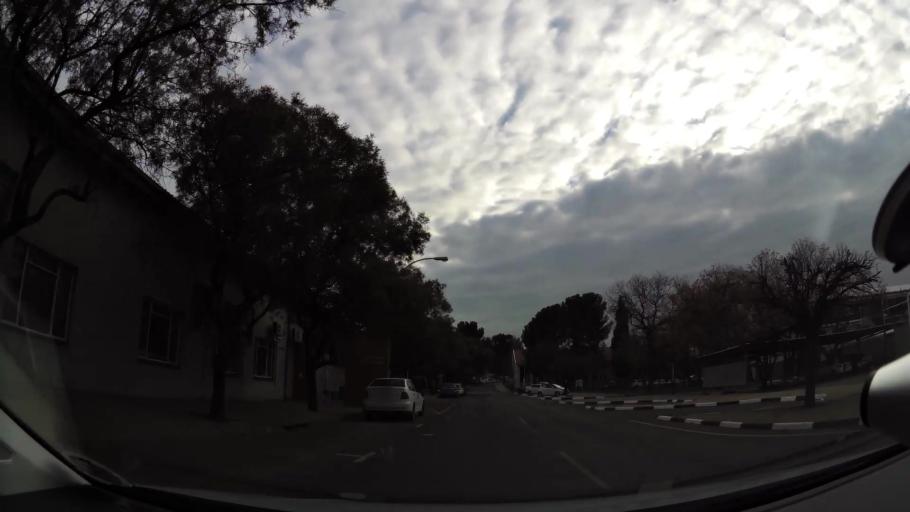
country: ZA
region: Orange Free State
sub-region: Mangaung Metropolitan Municipality
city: Bloemfontein
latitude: -29.1132
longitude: 26.1856
